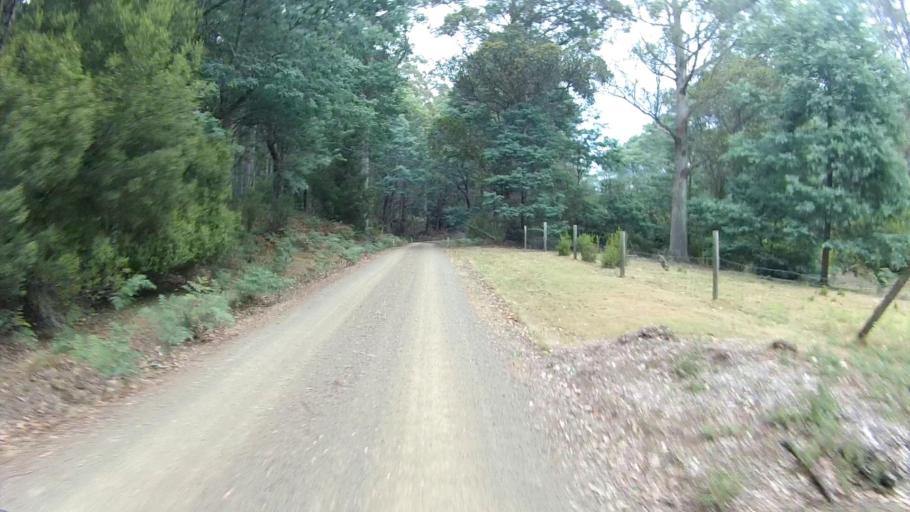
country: AU
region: Tasmania
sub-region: Kingborough
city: Kettering
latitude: -43.2122
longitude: 147.1790
